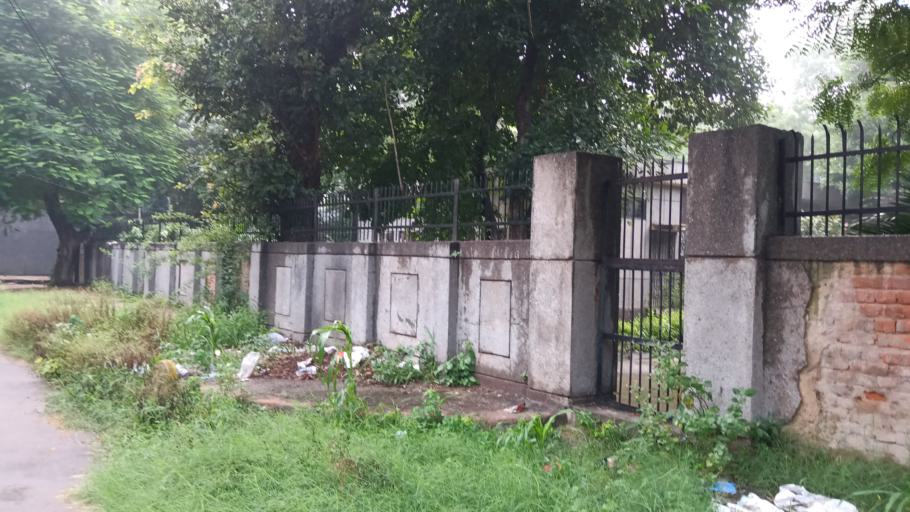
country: IN
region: NCT
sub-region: New Delhi
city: New Delhi
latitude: 28.5748
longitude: 77.2503
